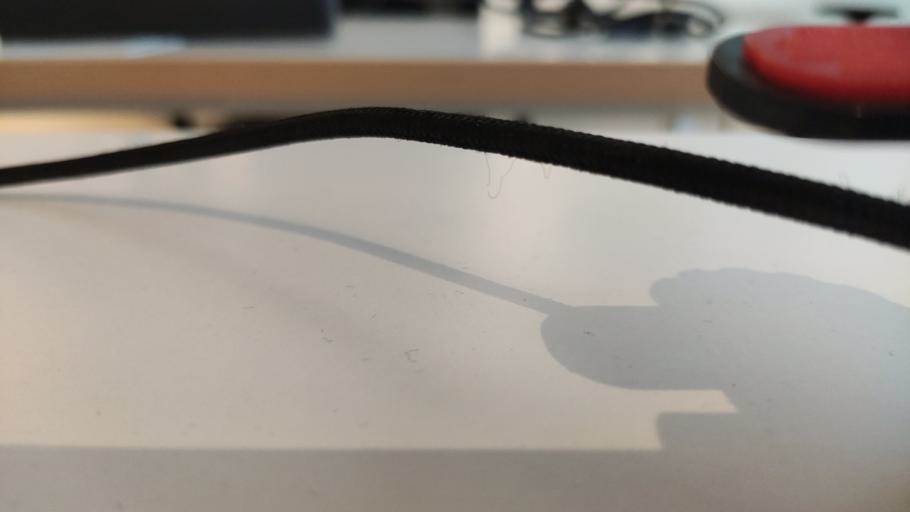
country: RU
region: Moskovskaya
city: Novopetrovskoye
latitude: 55.9491
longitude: 36.4374
